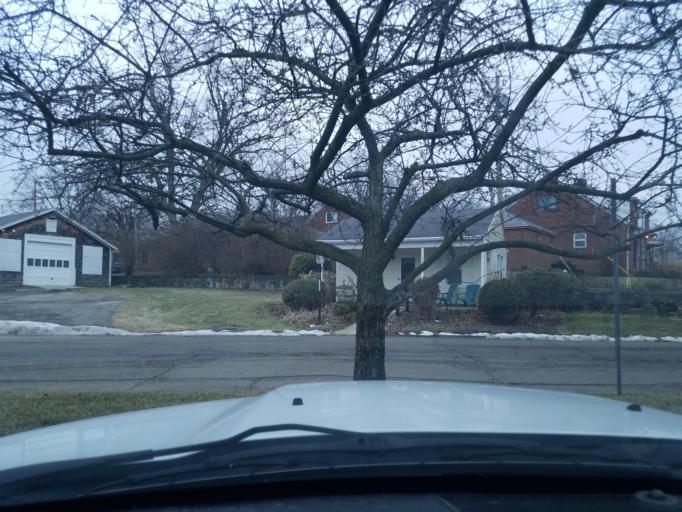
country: US
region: Ohio
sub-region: Montgomery County
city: Oakwood
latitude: 39.7180
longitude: -84.1605
